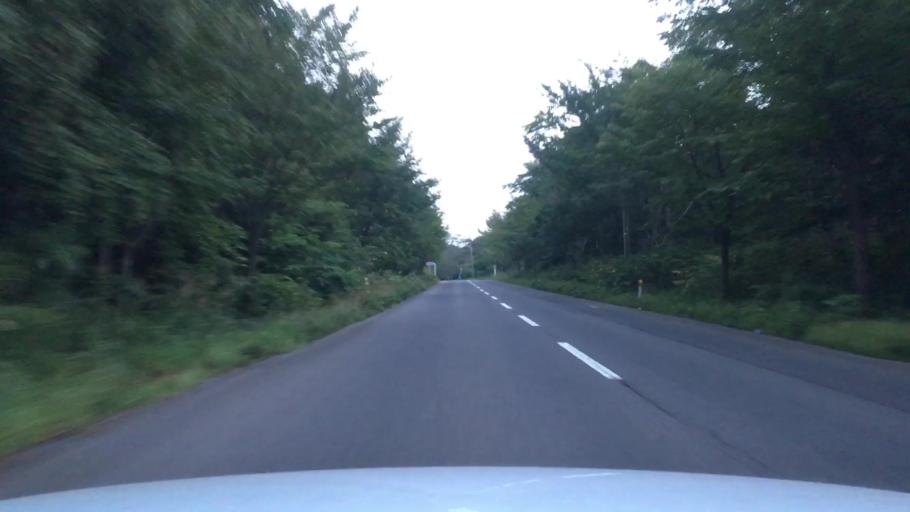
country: JP
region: Aomori
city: Shimokizukuri
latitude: 40.6895
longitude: 140.3624
